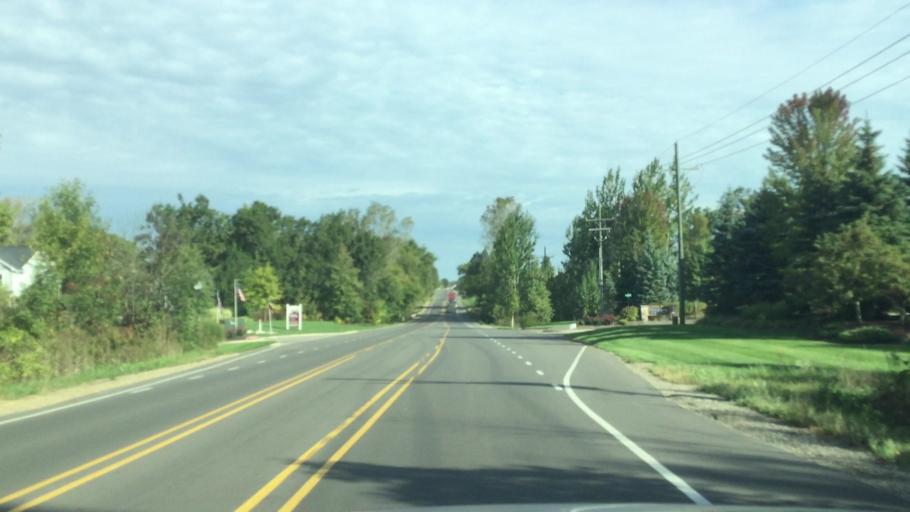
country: US
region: Michigan
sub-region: Livingston County
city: Howell
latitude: 42.6177
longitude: -83.8751
